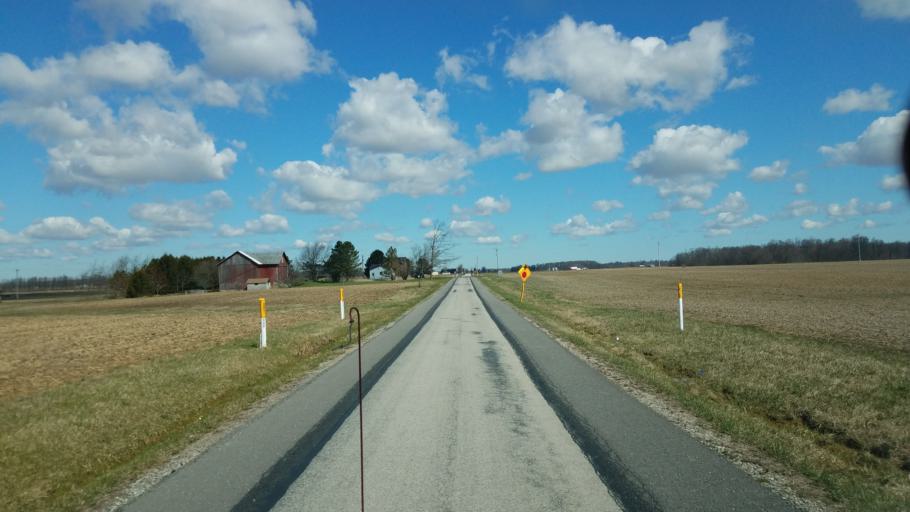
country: US
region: Ohio
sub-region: Sandusky County
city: Mount Carmel
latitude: 41.0930
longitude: -82.9383
